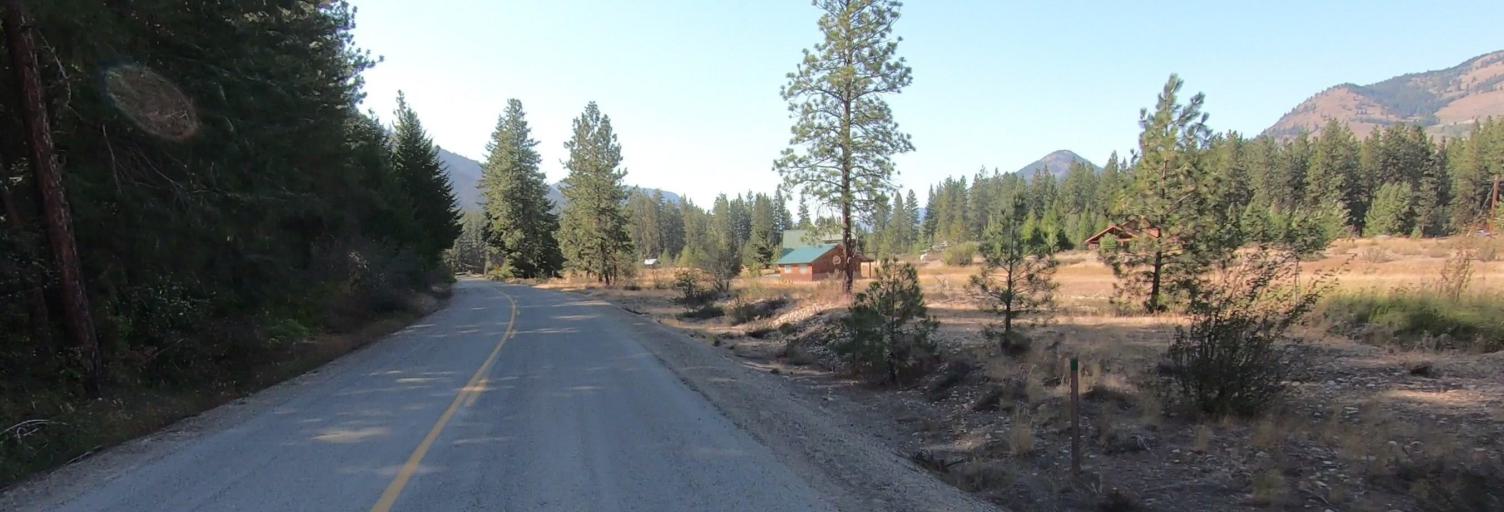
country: US
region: Washington
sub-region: Chelan County
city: Granite Falls
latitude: 48.4950
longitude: -120.2591
